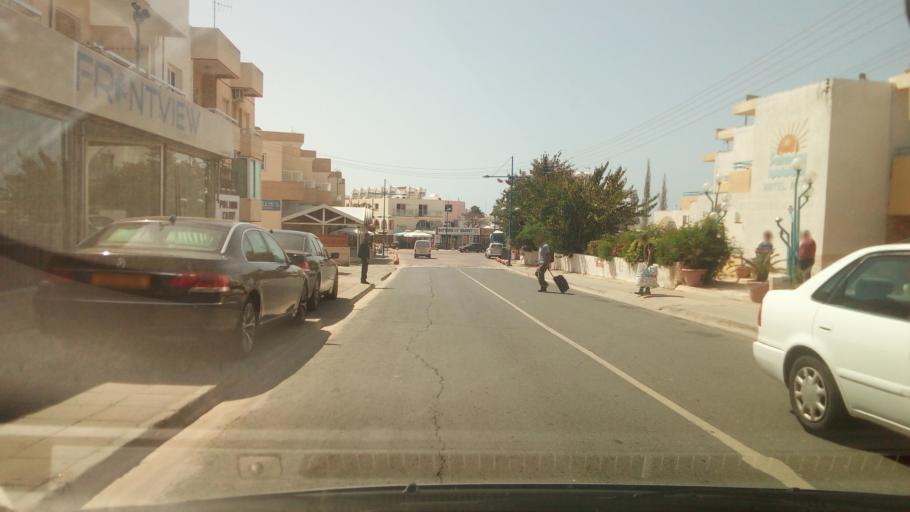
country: CY
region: Ammochostos
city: Ayia Napa
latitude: 34.9910
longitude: 33.9924
